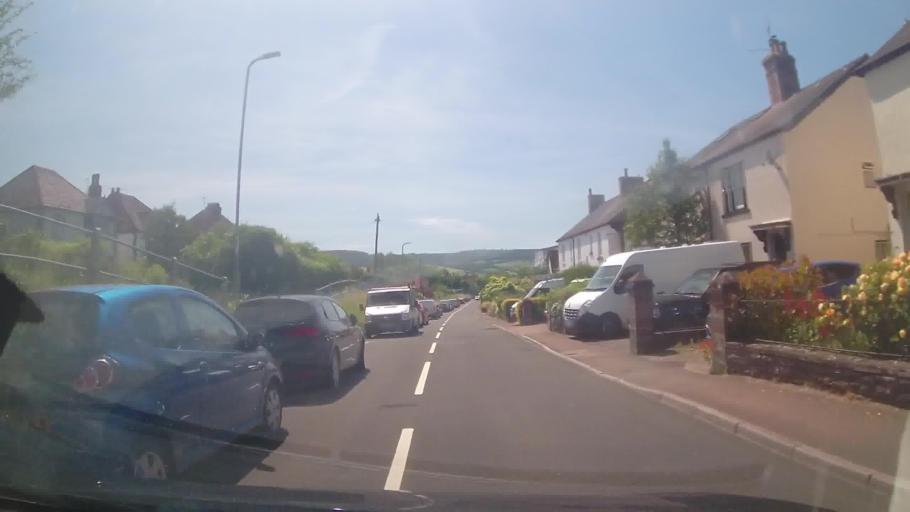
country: GB
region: Wales
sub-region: Monmouthshire
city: Monmouth
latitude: 51.8213
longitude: -2.7122
